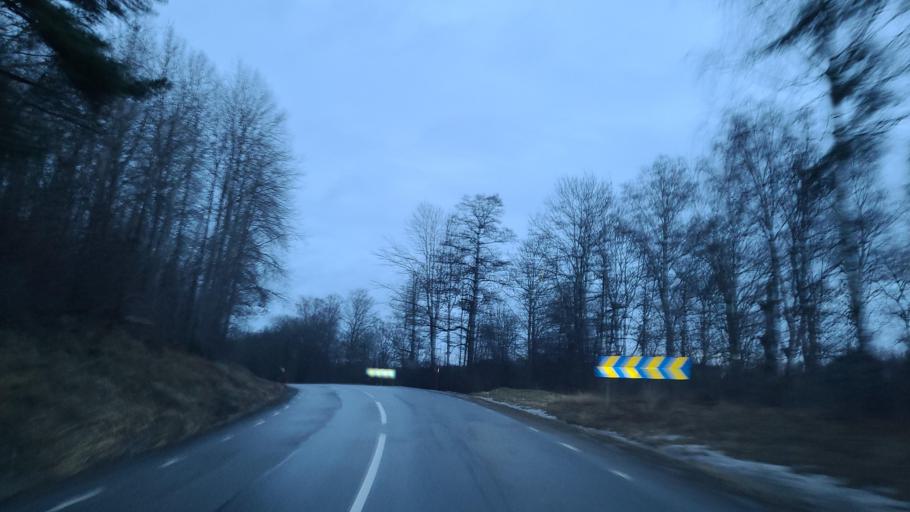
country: SE
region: Stockholm
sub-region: Norrtalje Kommun
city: Norrtalje
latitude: 59.7410
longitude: 18.6619
